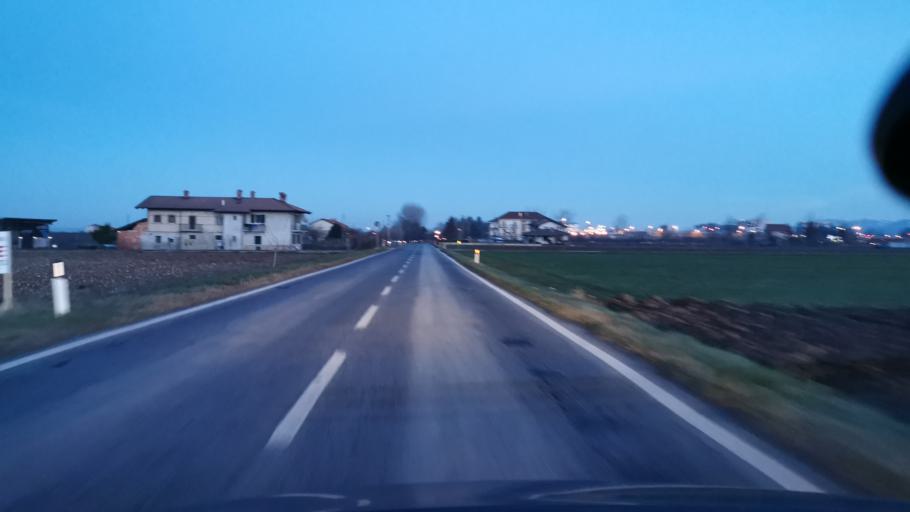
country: IT
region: Piedmont
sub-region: Provincia di Cuneo
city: Roata Rossi
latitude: 44.4423
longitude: 7.5577
